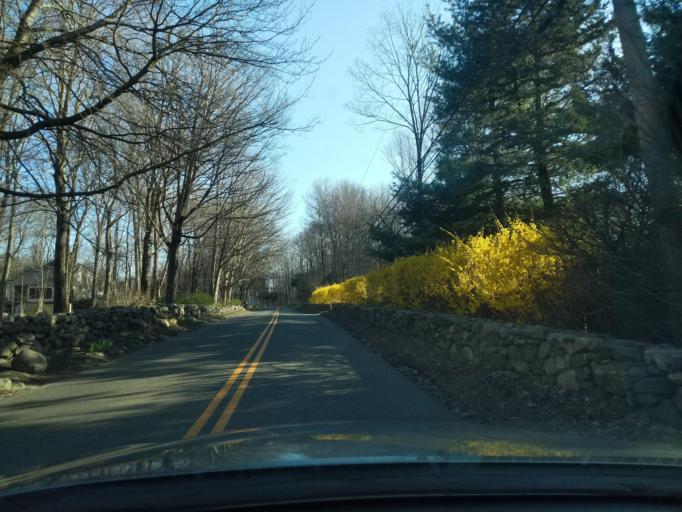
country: US
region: Connecticut
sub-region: Fairfield County
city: Newtown
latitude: 41.3747
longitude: -73.2917
